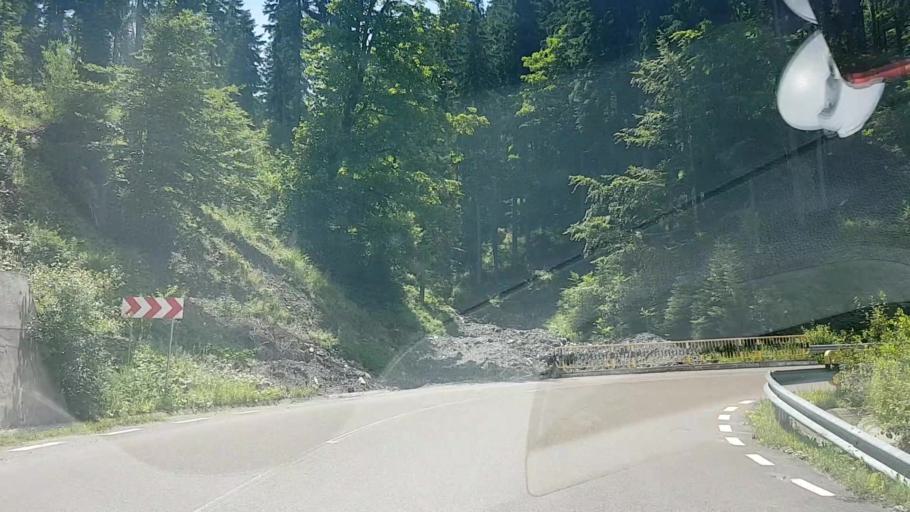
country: RO
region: Suceava
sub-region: Comuna Sadova
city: Sadova
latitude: 47.4634
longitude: 25.5171
